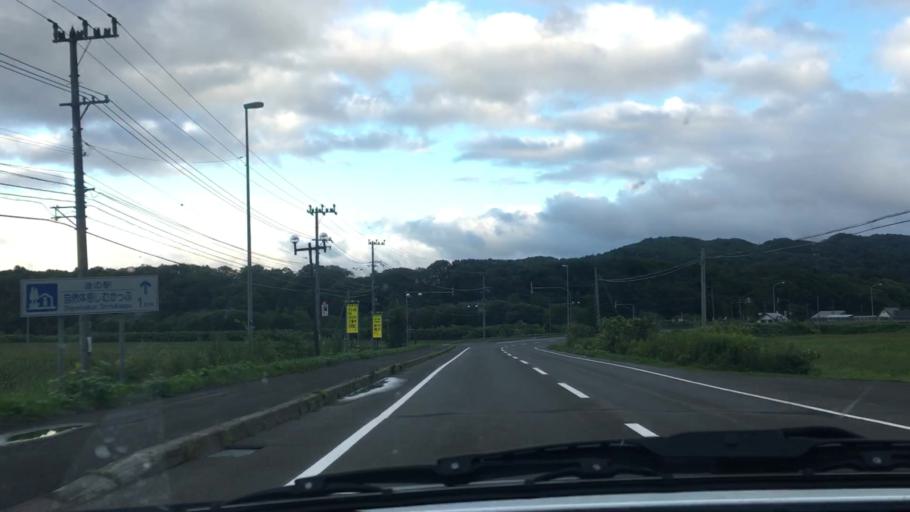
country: JP
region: Hokkaido
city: Shimo-furano
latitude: 42.9855
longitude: 142.3994
